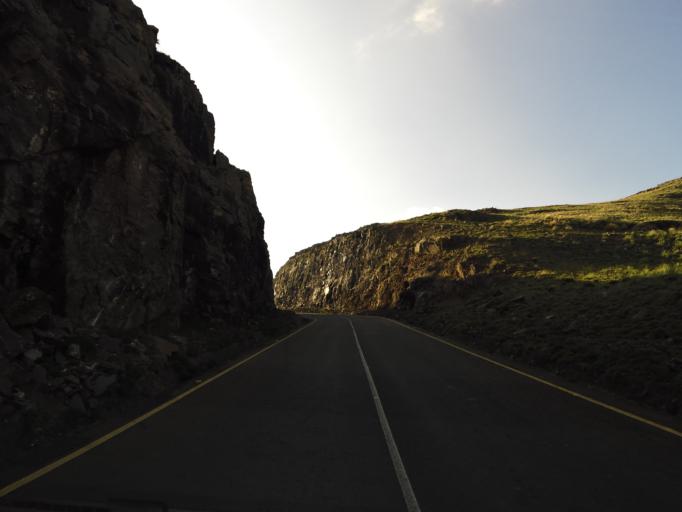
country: LS
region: Butha-Buthe
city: Butha-Buthe
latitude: -29.1039
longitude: 28.4276
